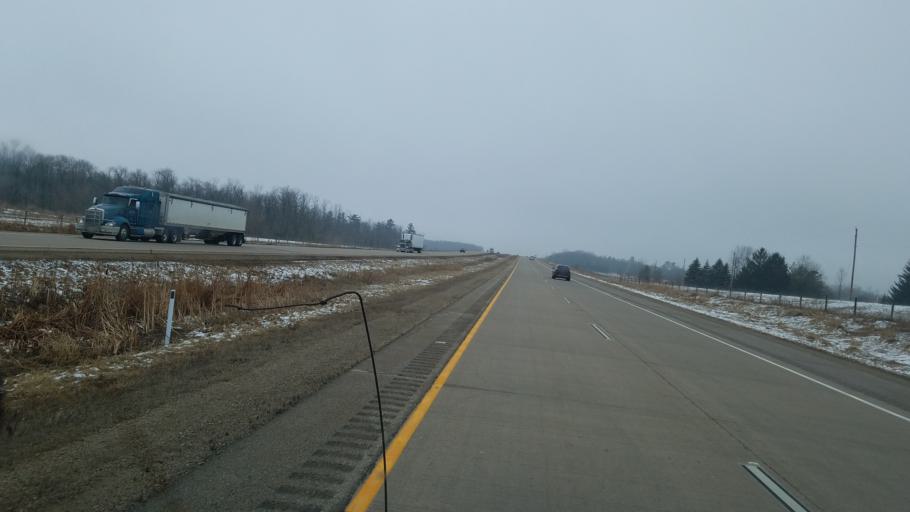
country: US
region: Wisconsin
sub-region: Winnebago County
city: Winneconne
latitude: 44.2343
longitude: -88.7575
